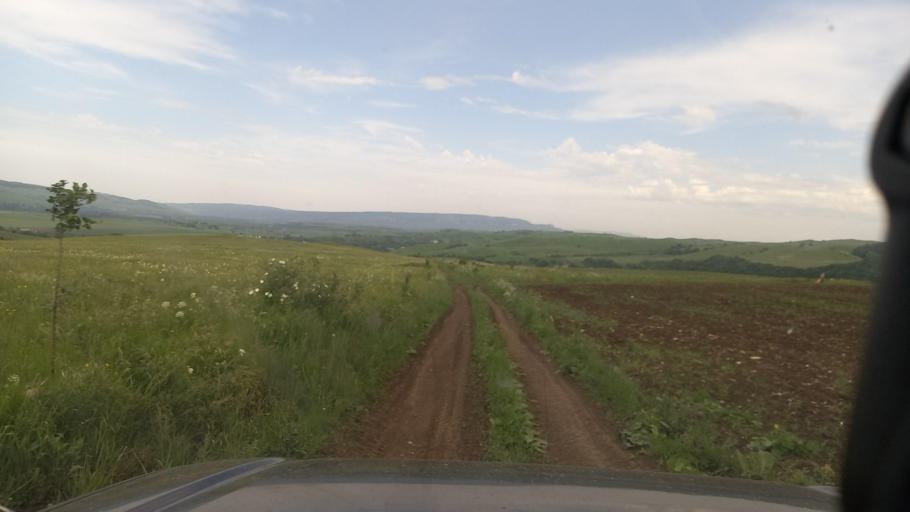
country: RU
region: Krasnodarskiy
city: Peredovaya
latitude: 44.0786
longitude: 41.3354
